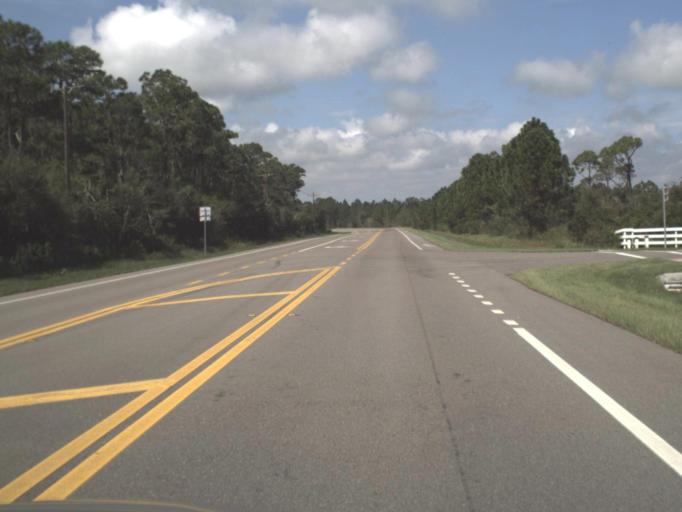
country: US
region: Florida
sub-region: Sarasota County
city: Lake Sarasota
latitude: 27.2457
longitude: -82.3550
